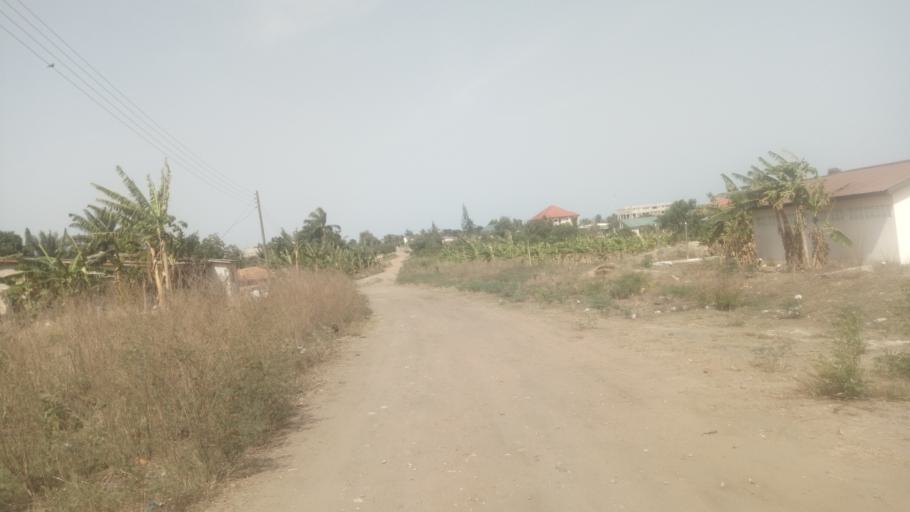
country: GH
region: Central
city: Winneba
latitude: 5.3775
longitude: -0.6501
